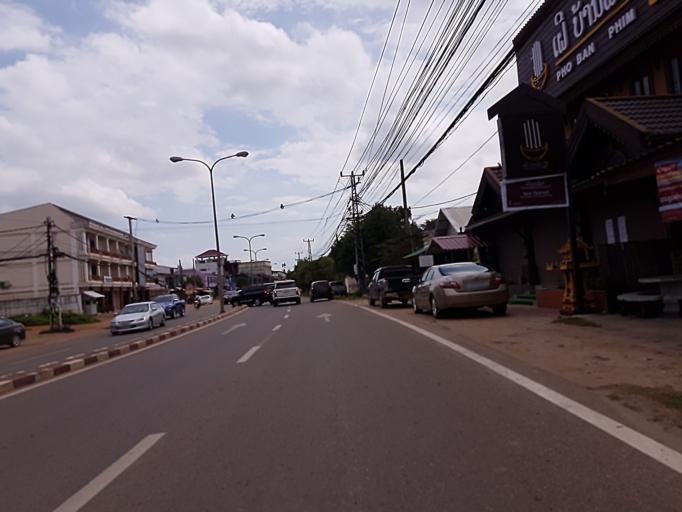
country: TH
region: Nong Khai
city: Si Chiang Mai
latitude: 17.9314
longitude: 102.6164
